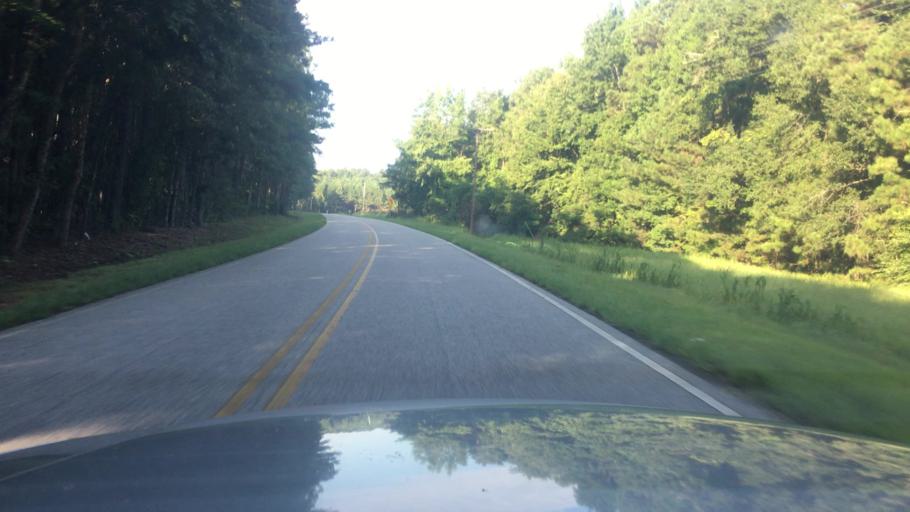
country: US
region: North Carolina
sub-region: Harnett County
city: Walkertown
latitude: 35.2255
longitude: -78.8903
